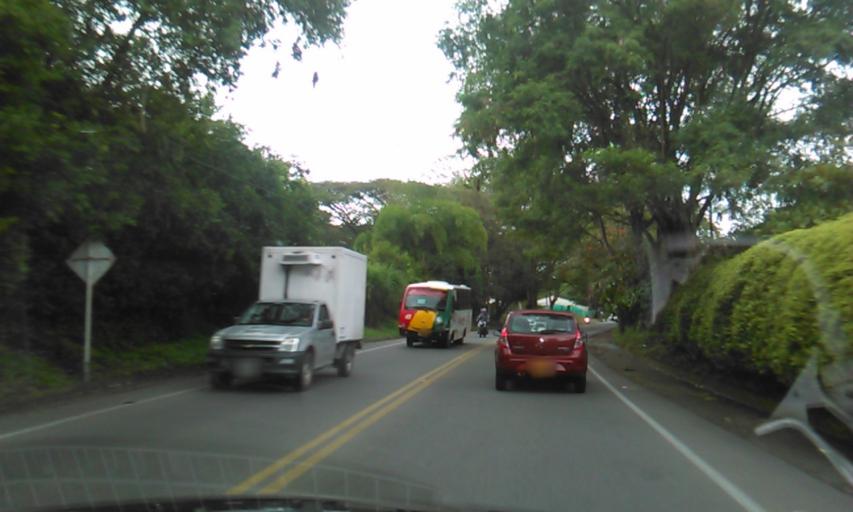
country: CO
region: Quindio
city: Montenegro
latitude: 4.5337
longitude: -75.7334
